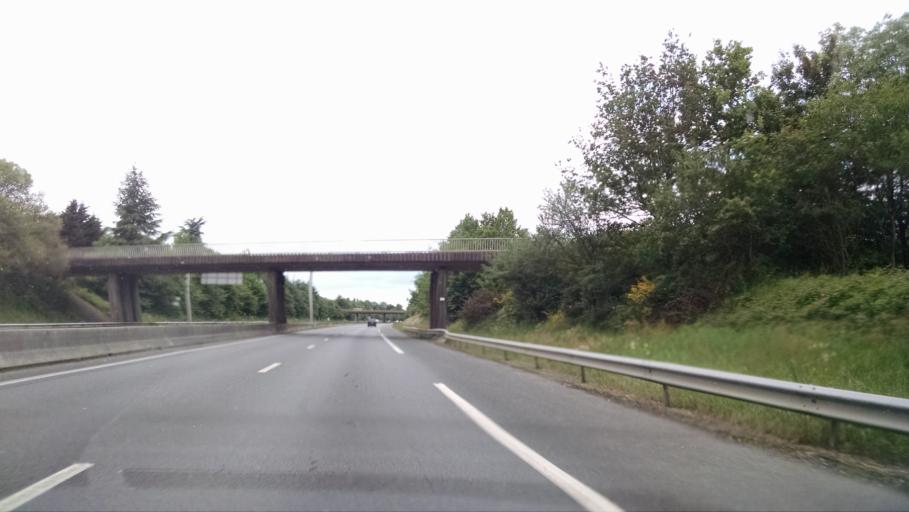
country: FR
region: Pays de la Loire
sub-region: Departement de la Loire-Atlantique
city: Les Sorinieres
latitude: 47.1355
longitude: -1.5100
